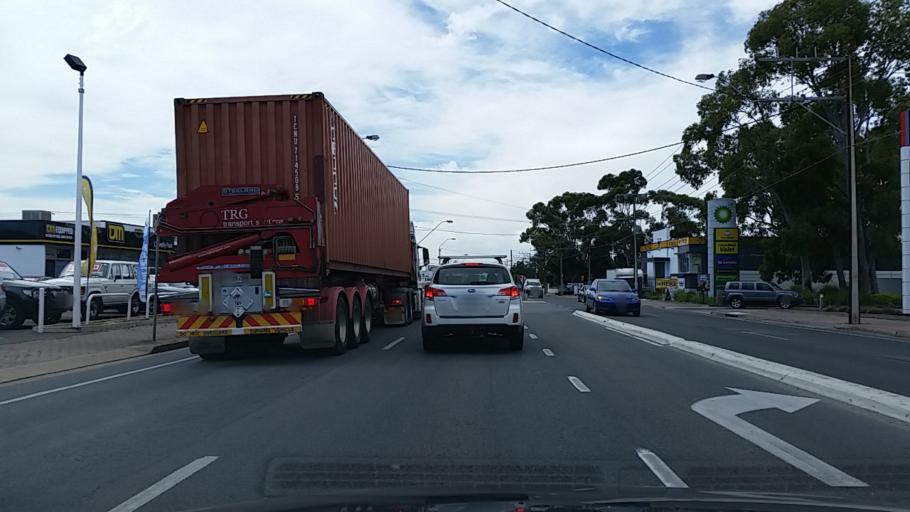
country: AU
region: South Australia
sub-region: Marion
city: Clovelly Park
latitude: -34.9979
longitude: 138.5752
